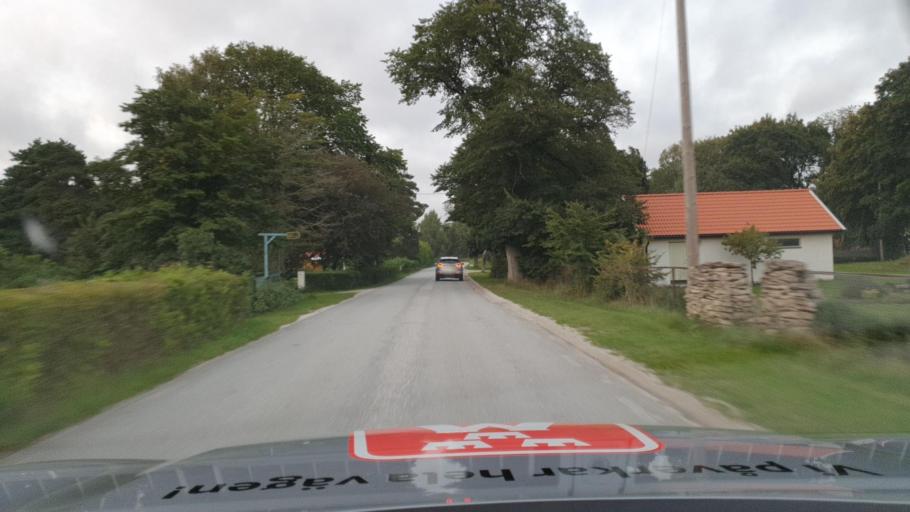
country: SE
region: Gotland
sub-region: Gotland
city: Hemse
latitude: 57.2857
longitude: 18.2715
